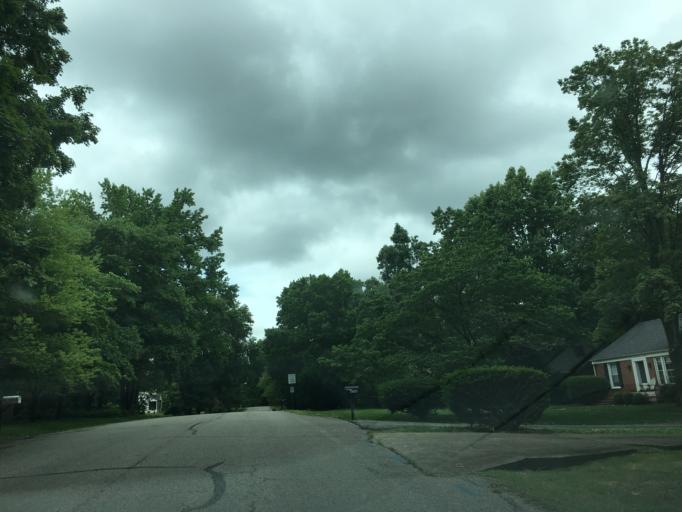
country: US
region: Tennessee
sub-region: Davidson County
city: Oak Hill
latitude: 36.1055
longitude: -86.7766
